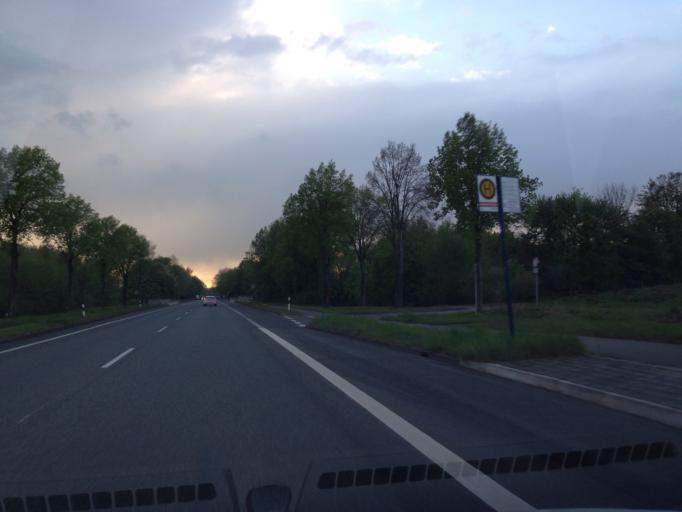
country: DE
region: North Rhine-Westphalia
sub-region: Regierungsbezirk Munster
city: Muenster
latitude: 51.9948
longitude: 7.5689
